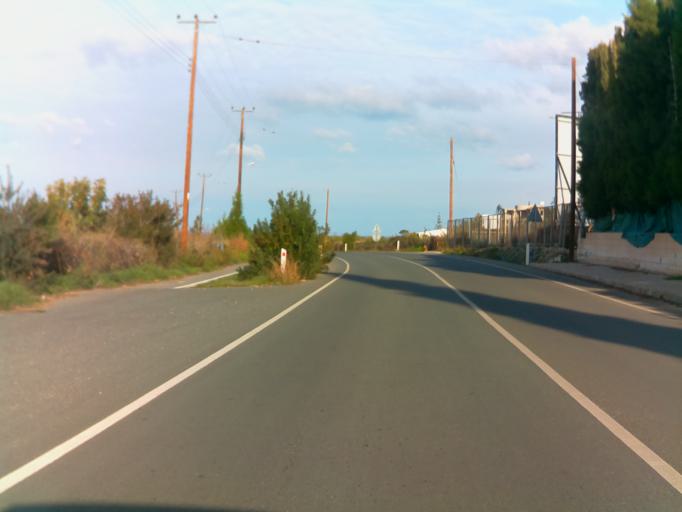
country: CY
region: Pafos
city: Pegeia
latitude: 34.8979
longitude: 32.3327
